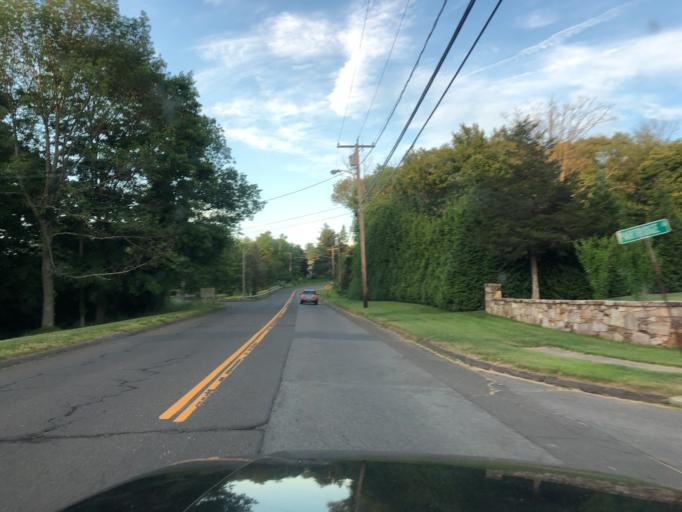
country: US
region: Connecticut
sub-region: Middlesex County
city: Middletown
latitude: 41.5659
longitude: -72.7175
